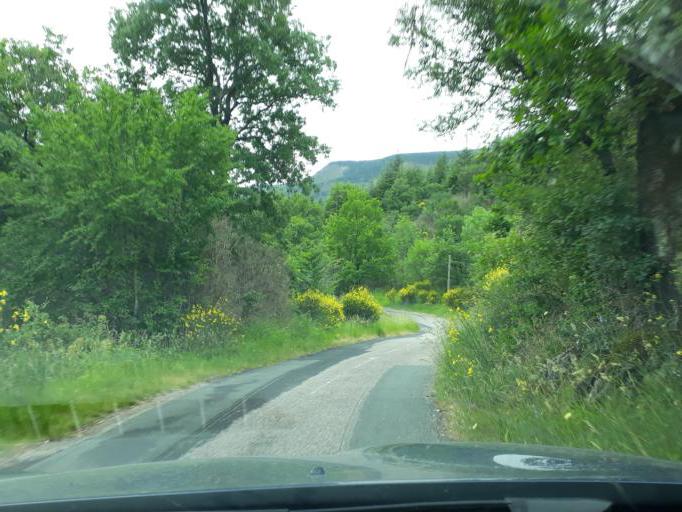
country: FR
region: Languedoc-Roussillon
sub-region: Departement de l'Herault
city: Lodeve
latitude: 43.7882
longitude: 3.2812
